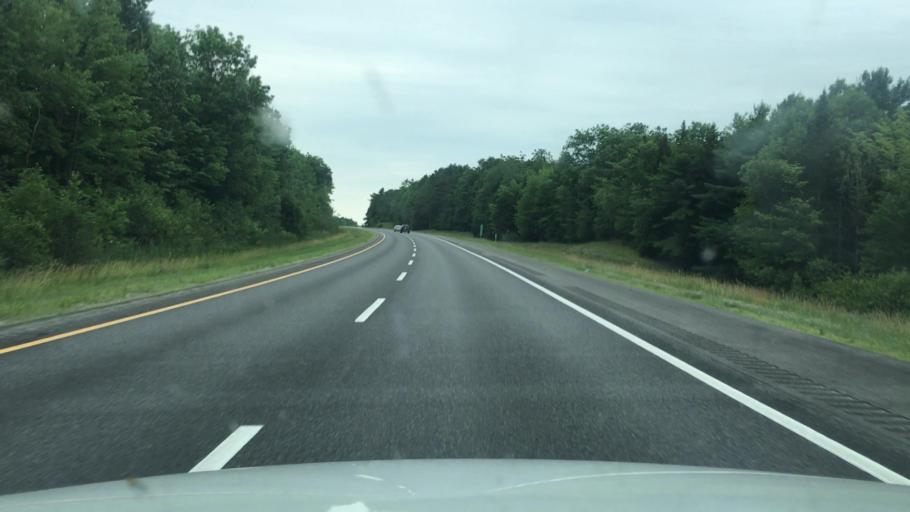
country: US
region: Maine
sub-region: Sagadahoc County
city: Topsham
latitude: 43.9920
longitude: -69.9393
